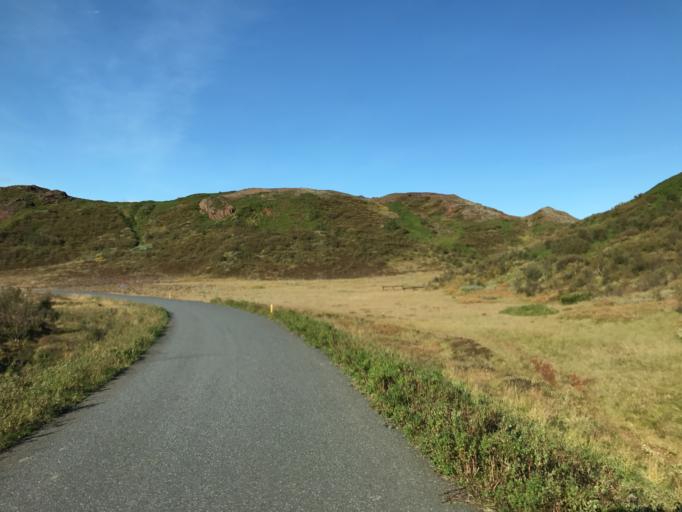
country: IS
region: South
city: Hveragerdi
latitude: 64.1365
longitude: -21.2505
